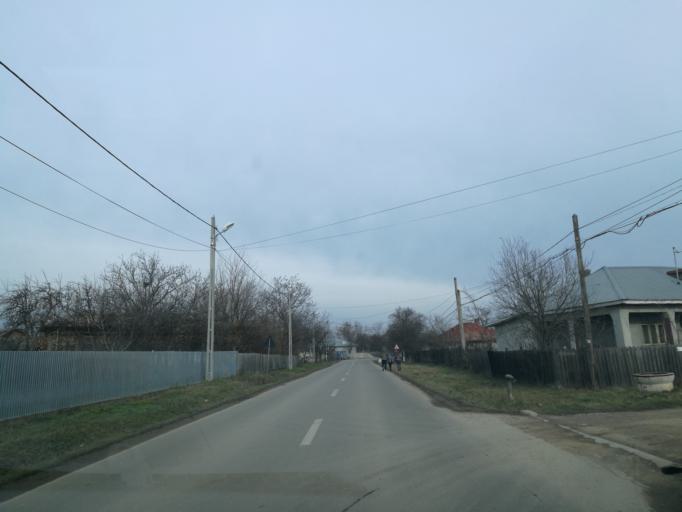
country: RO
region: Ialomita
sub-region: Comuna Fierbinti-Targ
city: Fierbintii de Jos
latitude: 44.6921
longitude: 26.3942
